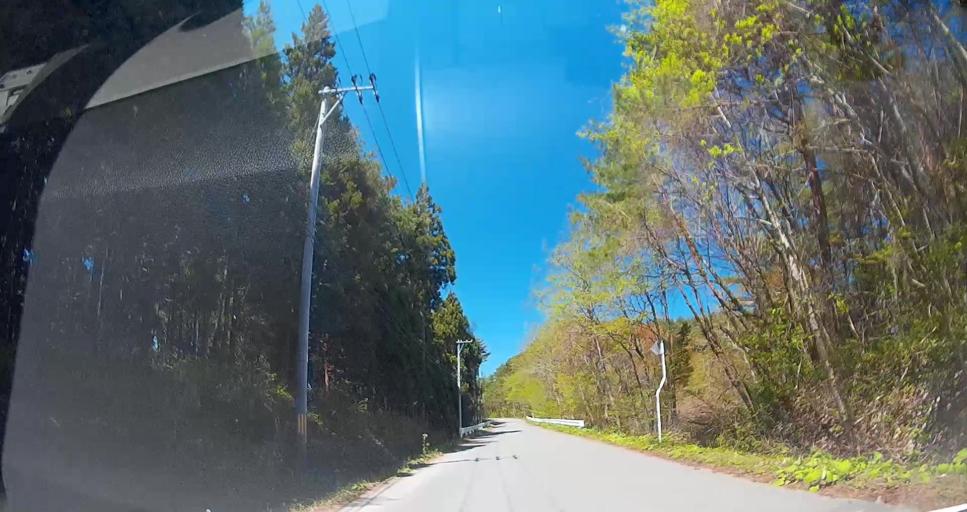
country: JP
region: Aomori
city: Mutsu
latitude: 41.2486
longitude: 141.3935
